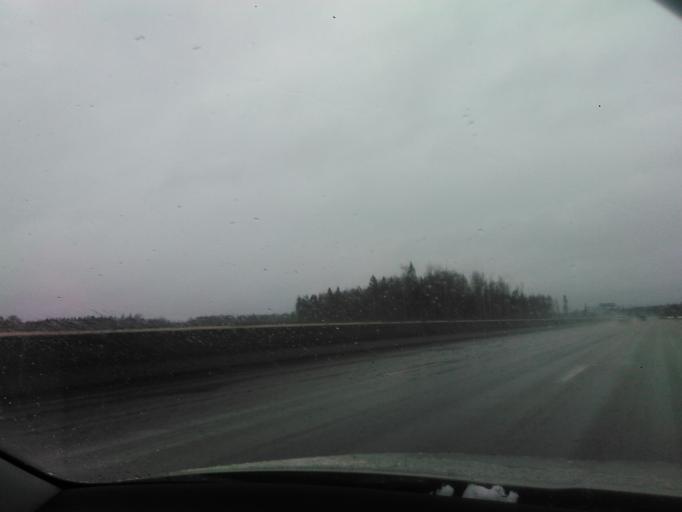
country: RU
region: Moskovskaya
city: Skhodnya
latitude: 55.9943
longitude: 37.3000
